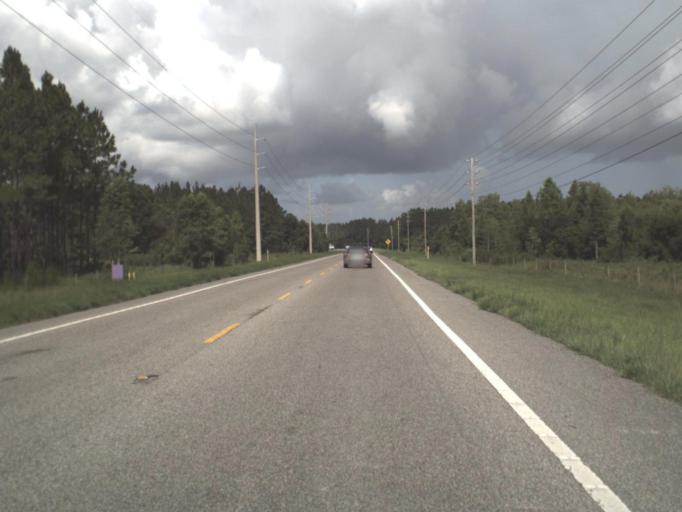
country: US
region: Florida
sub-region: Pasco County
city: Land O' Lakes
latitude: 28.3230
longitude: -82.4238
